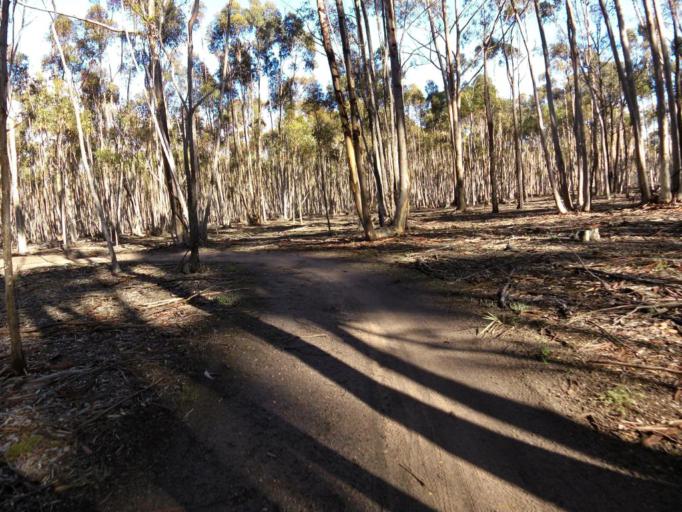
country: AU
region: Victoria
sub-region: Greater Geelong
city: Lara
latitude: -37.9568
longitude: 144.4042
